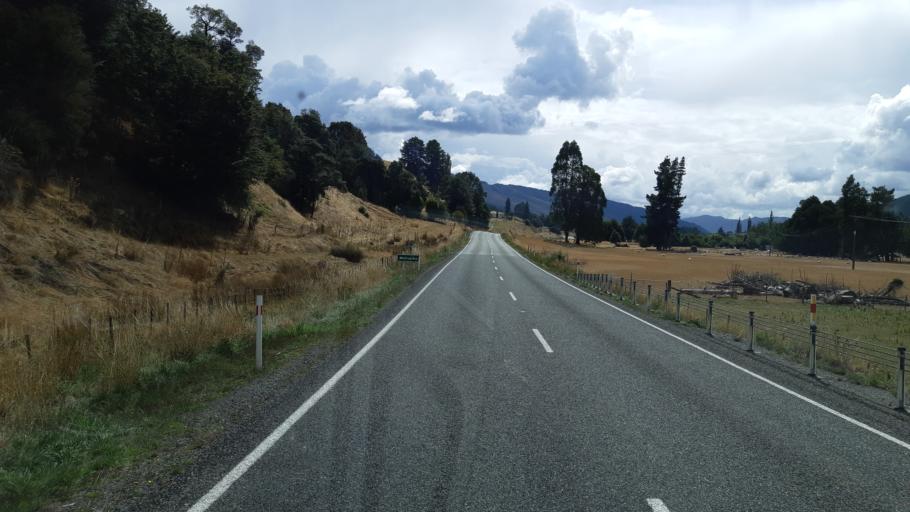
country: NZ
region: Tasman
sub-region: Tasman District
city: Wakefield
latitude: -41.4916
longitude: 172.7979
